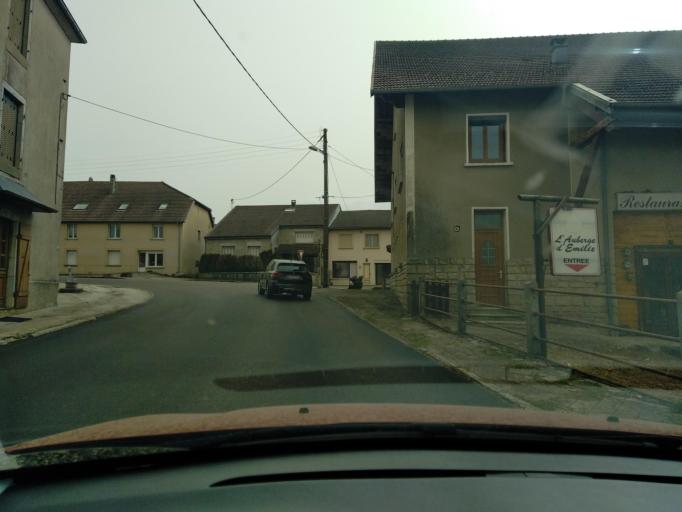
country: FR
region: Franche-Comte
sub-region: Departement du Jura
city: Champagnole
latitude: 46.7509
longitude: 5.8144
